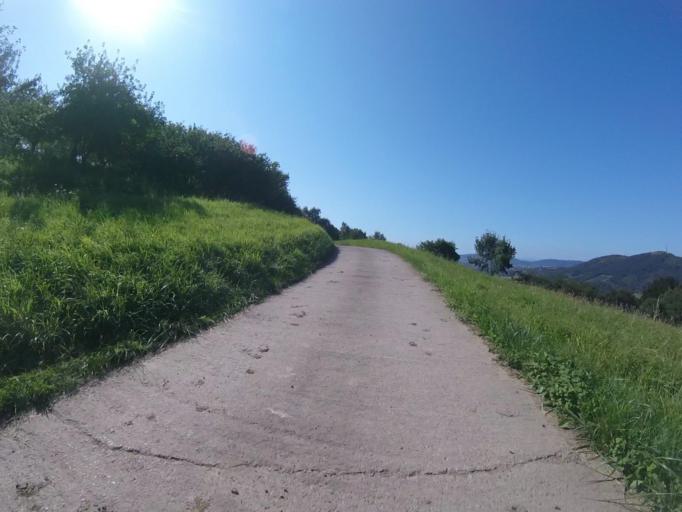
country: ES
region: Basque Country
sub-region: Provincia de Guipuzcoa
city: Astigarraga
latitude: 43.2725
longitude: -1.9252
